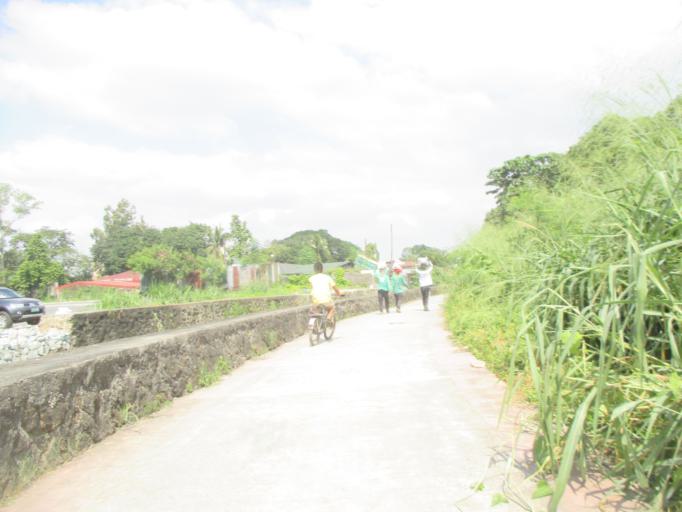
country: PH
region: Metro Manila
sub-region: Marikina
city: Calumpang
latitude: 14.6354
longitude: 121.1030
